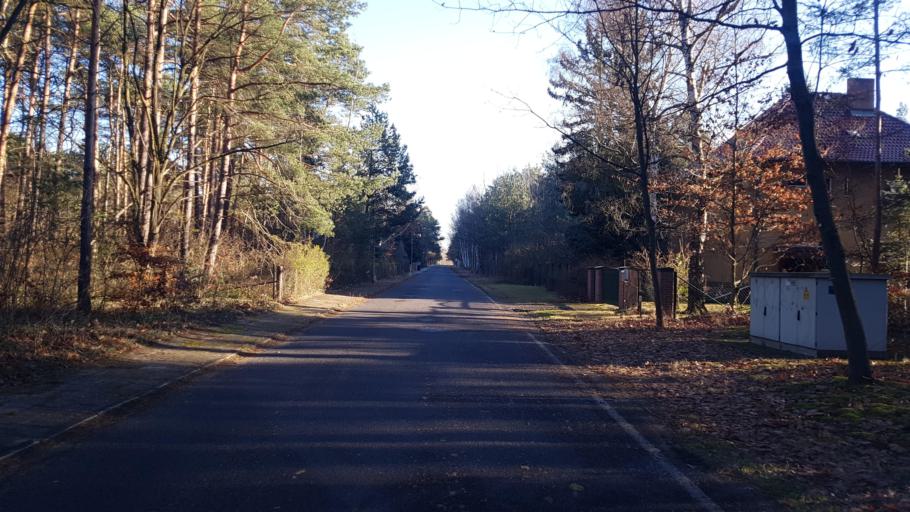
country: DE
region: Brandenburg
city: Heinersbruck
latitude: 51.7416
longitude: 14.5162
